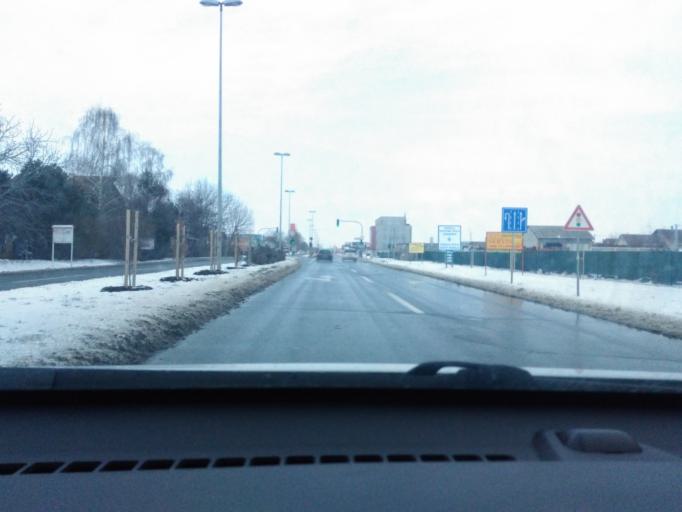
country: RS
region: Autonomna Pokrajina Vojvodina
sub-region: Juznobacki Okrug
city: Novi Sad
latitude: 45.2952
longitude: 19.8307
